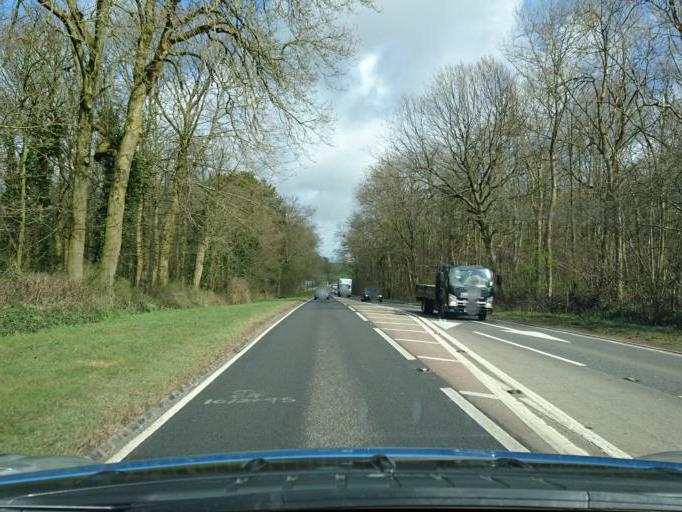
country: GB
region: England
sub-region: South Gloucestershire
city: Hinton
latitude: 51.4812
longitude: -2.3619
